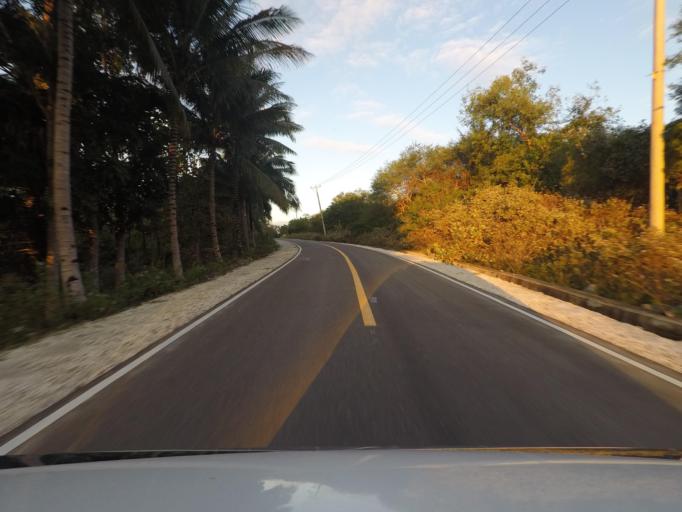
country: TL
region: Lautem
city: Lospalos
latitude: -8.3983
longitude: 127.2760
